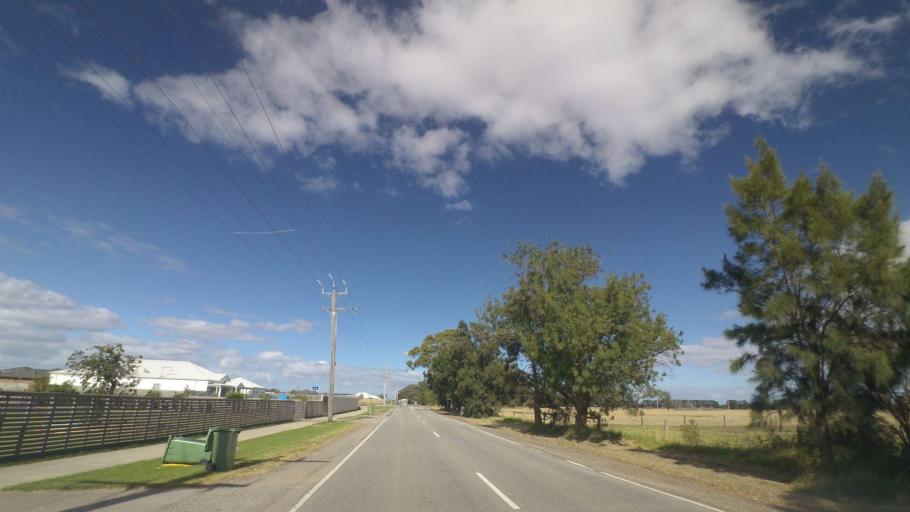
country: AU
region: Victoria
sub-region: Cardinia
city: Koo-Wee-Rup
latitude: -38.2022
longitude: 145.4840
